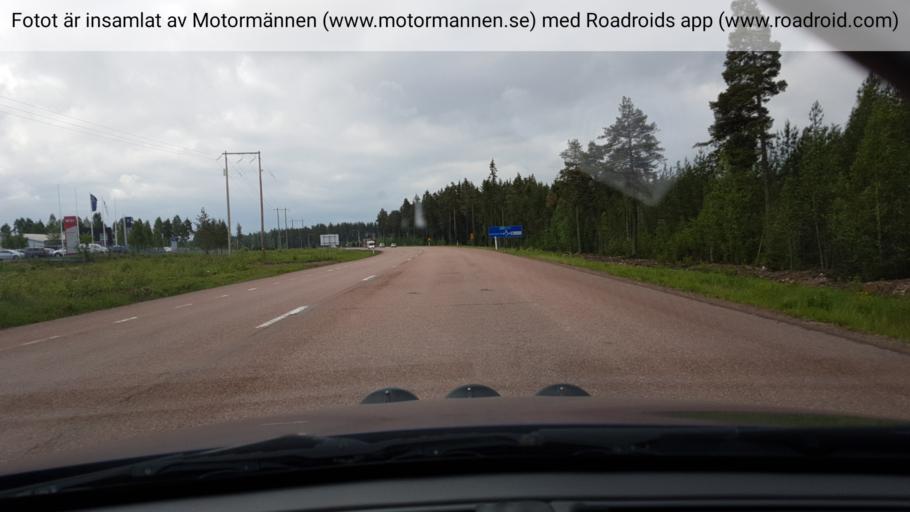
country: SE
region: Dalarna
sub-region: Mora Kommun
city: Mora
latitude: 61.0205
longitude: 14.5885
